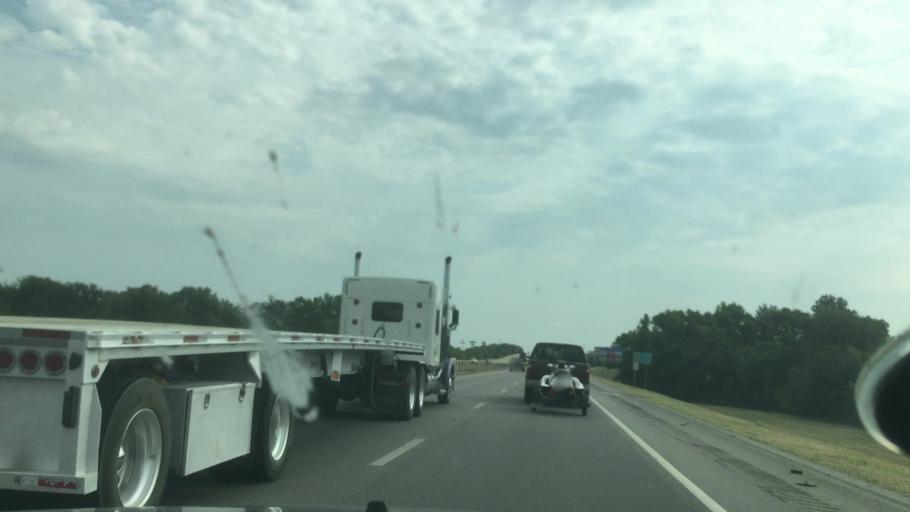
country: US
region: Oklahoma
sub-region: Bryan County
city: Durant
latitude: 33.9887
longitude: -96.4103
